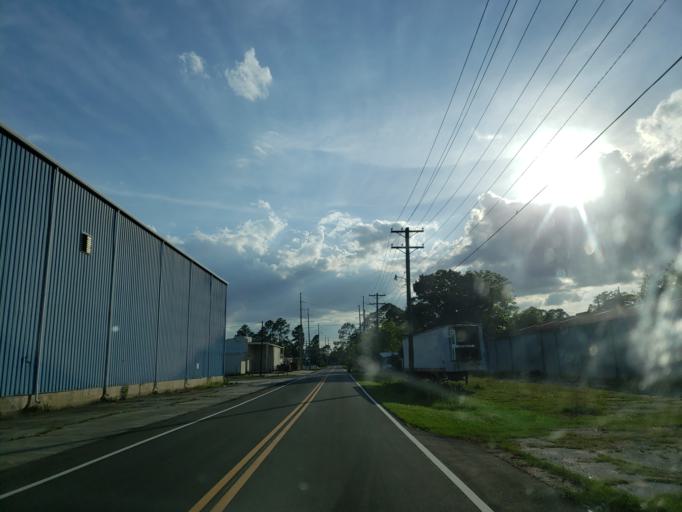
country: US
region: Georgia
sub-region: Cook County
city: Adel
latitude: 31.1374
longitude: -83.4272
